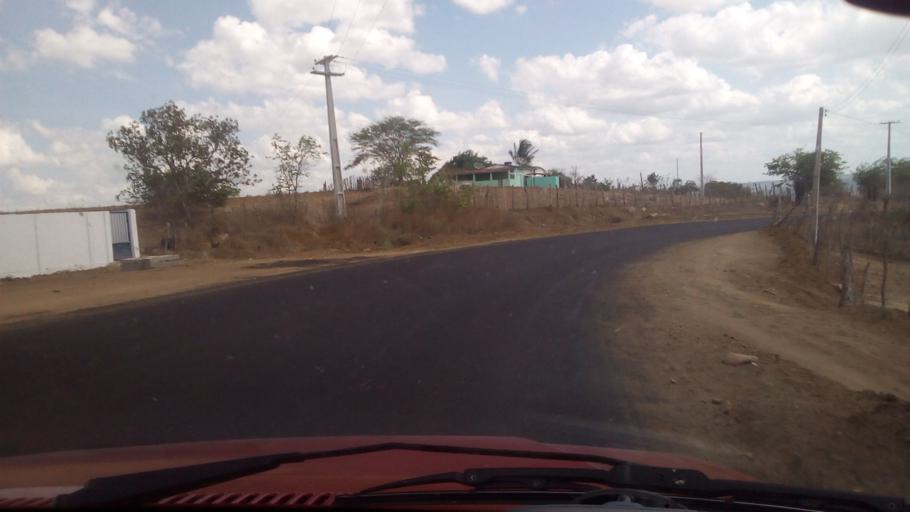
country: BR
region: Paraiba
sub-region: Cacimba De Dentro
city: Cacimba de Dentro
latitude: -6.6534
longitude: -35.7699
